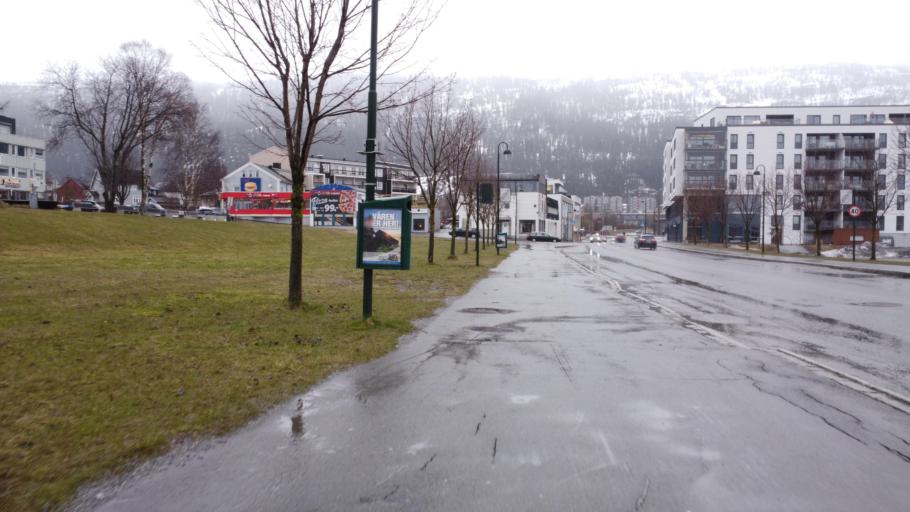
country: NO
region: Nordland
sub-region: Rana
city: Mo i Rana
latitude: 66.3092
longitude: 14.1354
